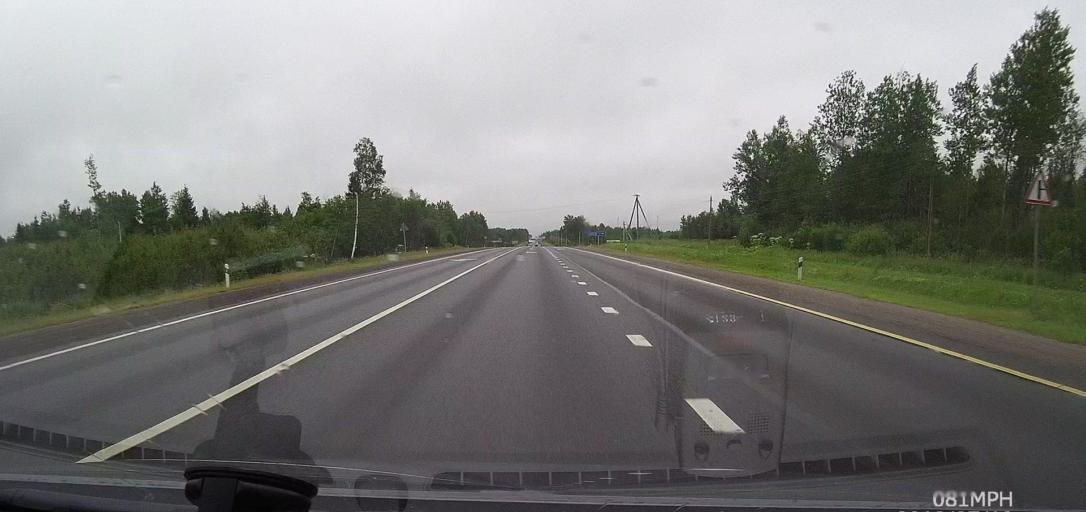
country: RU
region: Leningrad
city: Staraya Ladoga
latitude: 59.9993
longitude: 32.1093
